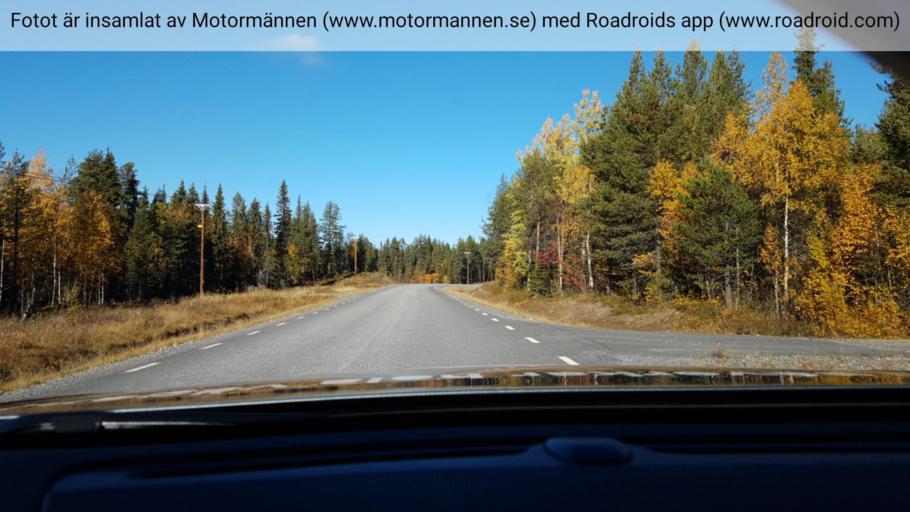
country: SE
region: Norrbotten
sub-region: Gallivare Kommun
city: Gaellivare
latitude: 66.8295
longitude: 21.0396
